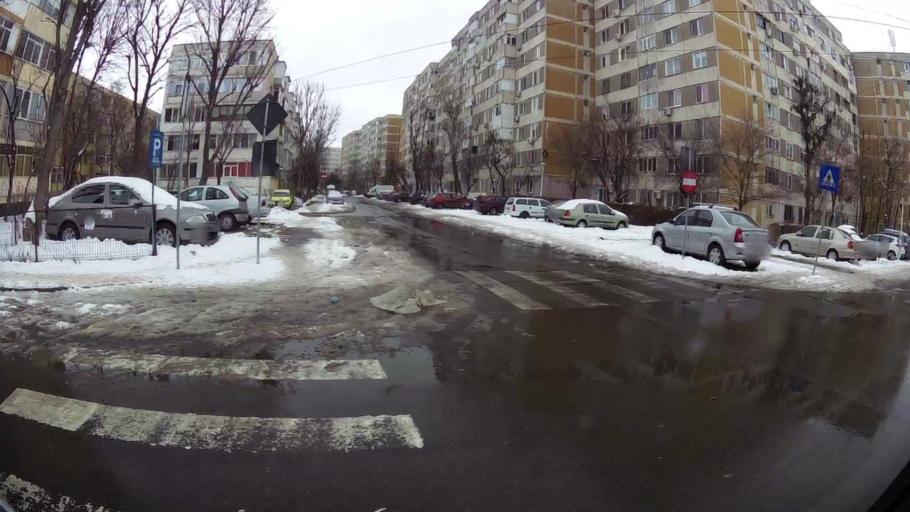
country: RO
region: Ilfov
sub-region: Comuna Popesti-Leordeni
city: Popesti-Leordeni
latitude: 44.3861
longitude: 26.1337
